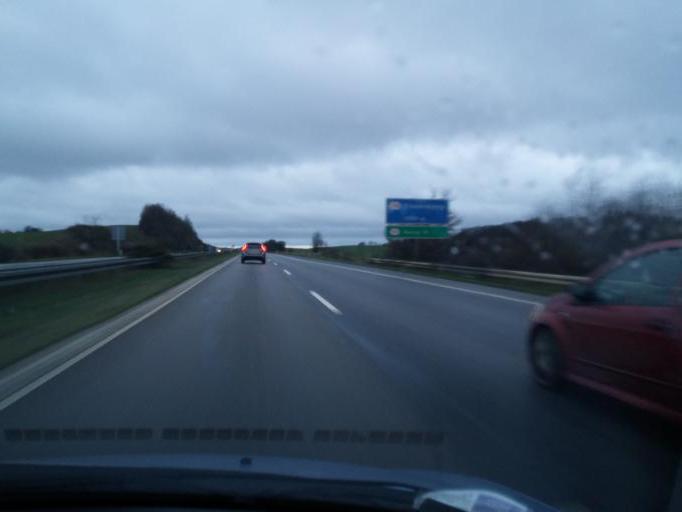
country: DK
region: South Denmark
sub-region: Assens Kommune
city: Vissenbjerg
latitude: 55.3964
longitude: 10.1811
